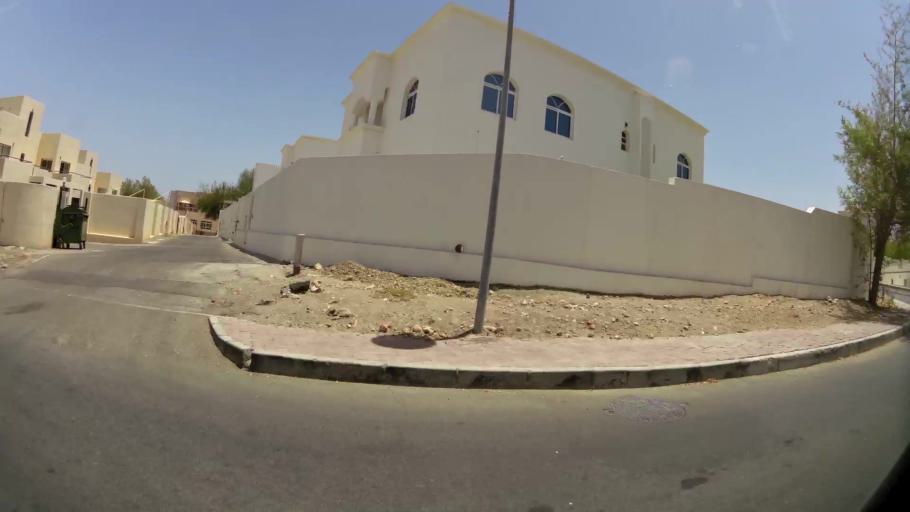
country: OM
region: Muhafazat Masqat
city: Bawshar
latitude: 23.6079
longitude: 58.4661
